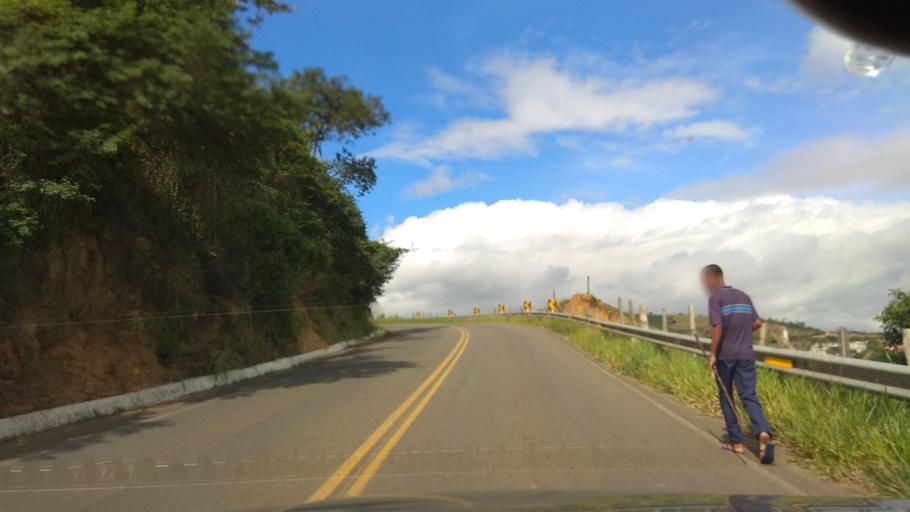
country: BR
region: Bahia
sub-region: Ubaira
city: Ubaira
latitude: -13.2544
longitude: -39.6639
